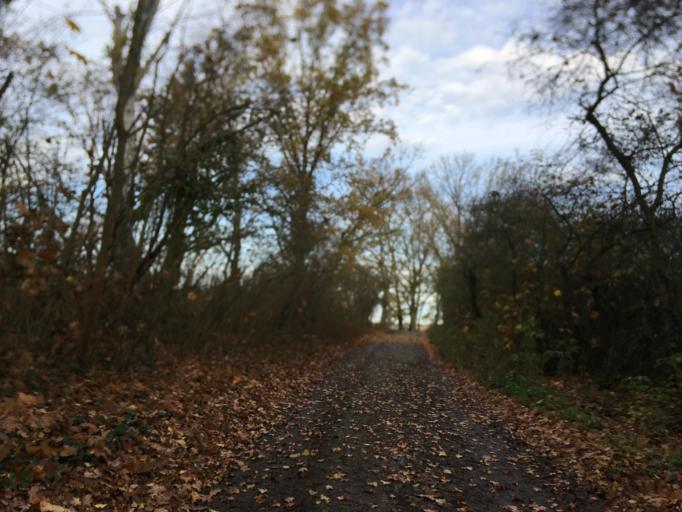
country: DE
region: Brandenburg
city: Schlepzig
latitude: 52.0351
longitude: 13.8336
